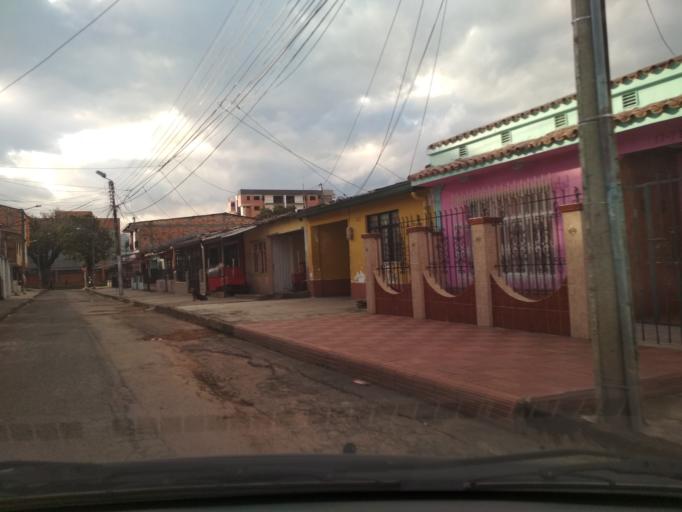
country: CO
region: Cauca
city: Popayan
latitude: 2.4396
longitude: -76.6168
